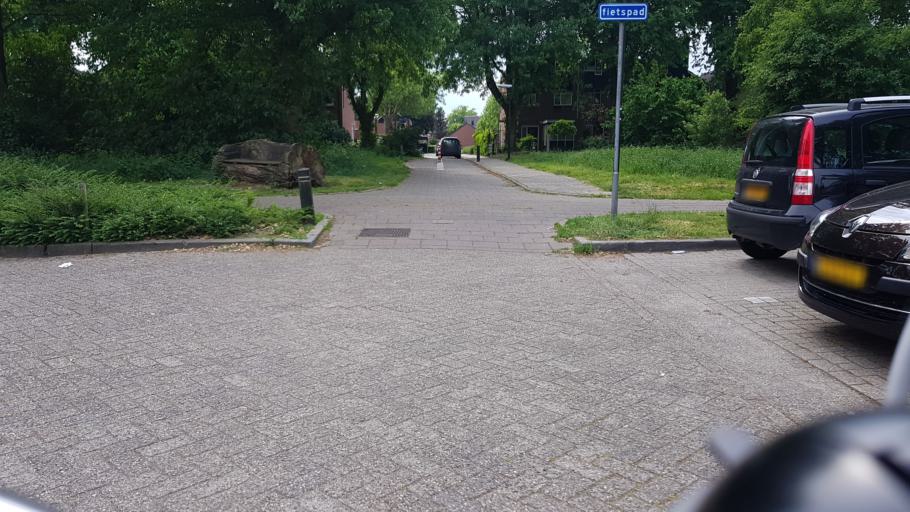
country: NL
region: Gelderland
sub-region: Gemeente Apeldoorn
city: Apeldoorn
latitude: 52.1885
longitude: 6.0000
